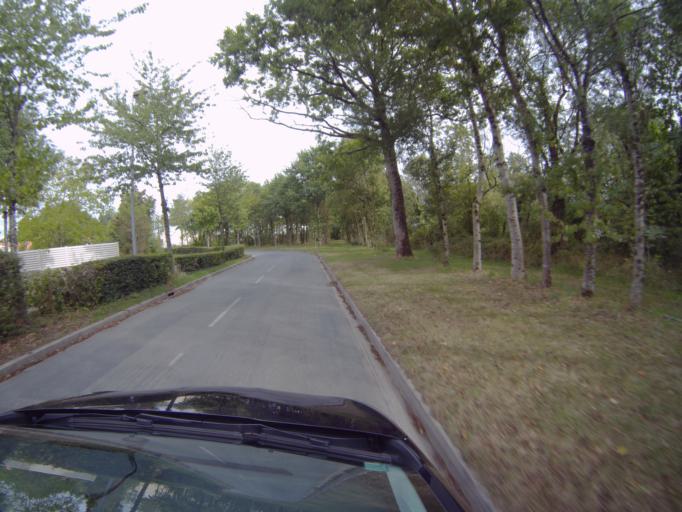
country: FR
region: Pays de la Loire
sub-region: Departement de la Vendee
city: Saint-Hilaire-de-Loulay
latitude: 46.9956
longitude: -1.3320
